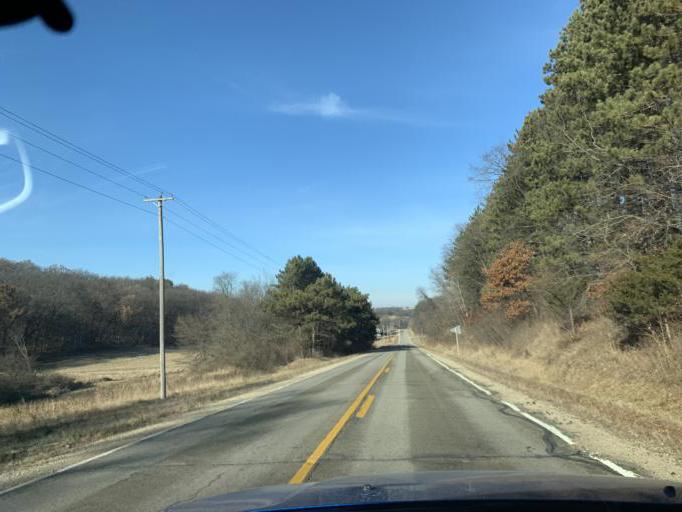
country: US
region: Wisconsin
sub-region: Green County
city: New Glarus
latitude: 42.7557
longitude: -89.8584
